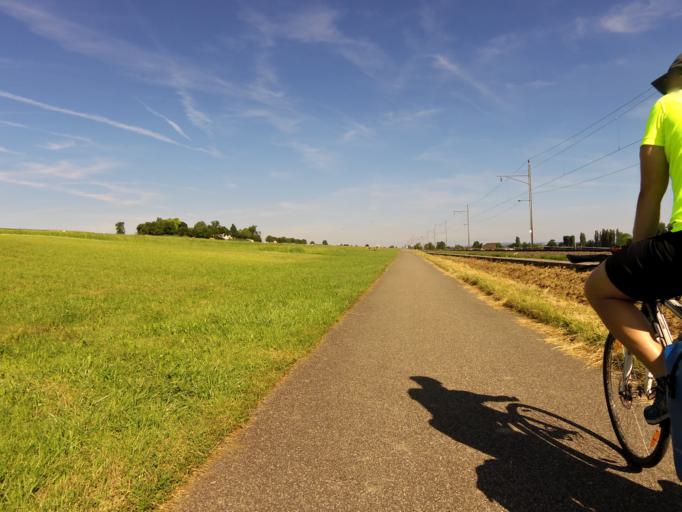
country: CH
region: Thurgau
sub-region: Kreuzlingen District
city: Guttingen
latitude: 47.6140
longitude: 9.2823
